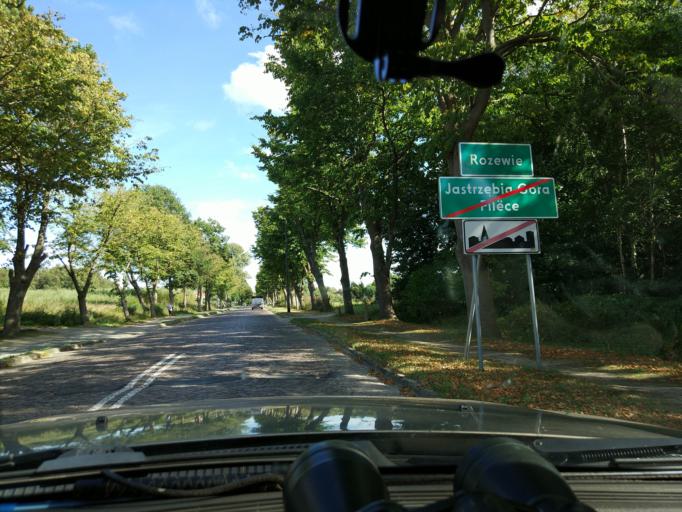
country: PL
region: Pomeranian Voivodeship
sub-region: Powiat pucki
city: Jastrzebia Gora
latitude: 54.8294
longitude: 18.3317
